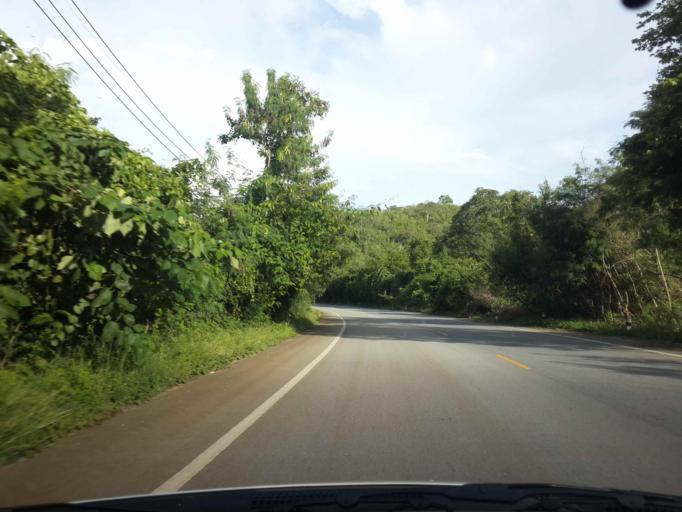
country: TH
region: Kanchanaburi
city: Sai Yok
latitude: 13.9283
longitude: 99.1146
